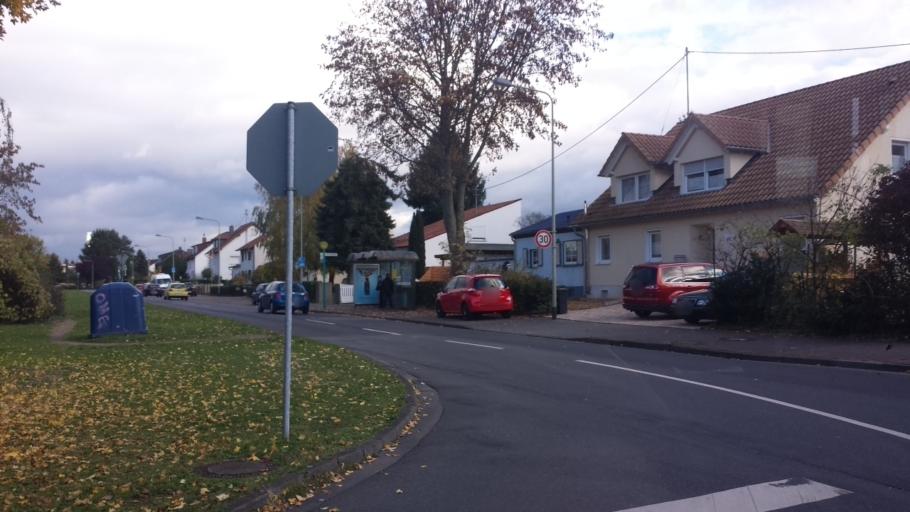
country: DE
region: Hesse
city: Niederrad
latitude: 50.0862
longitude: 8.6043
